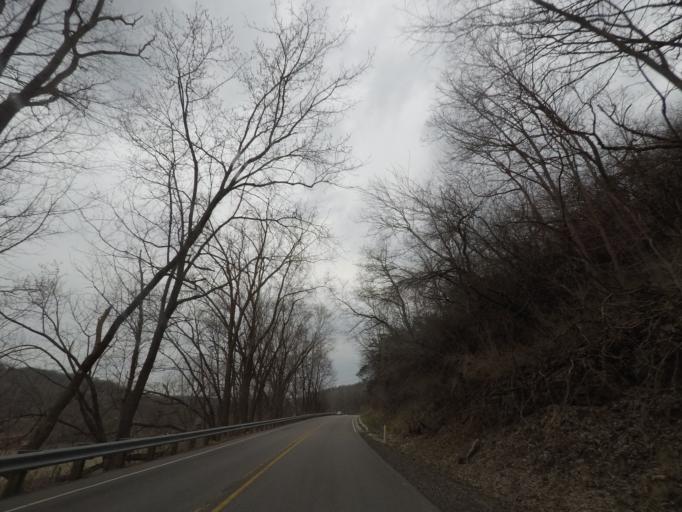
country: US
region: Wisconsin
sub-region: Dane County
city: Cross Plains
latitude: 43.1037
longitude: -89.5941
